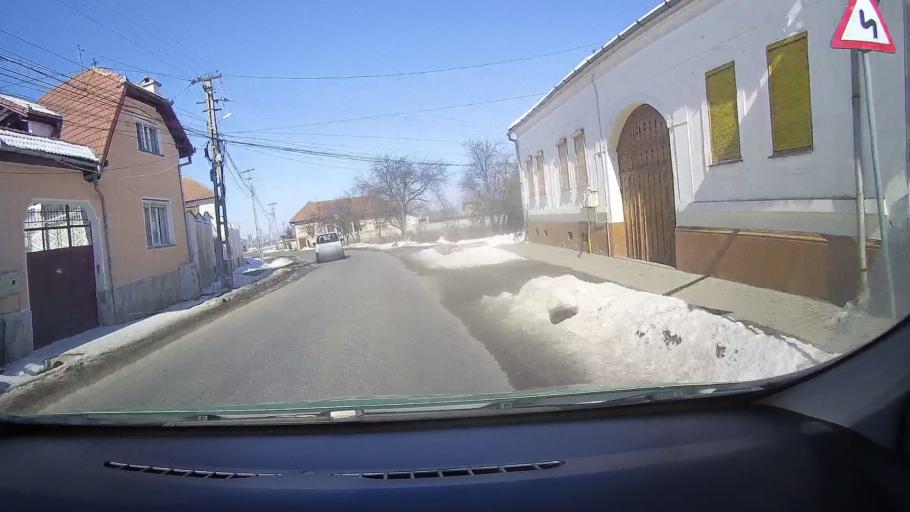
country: RO
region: Brasov
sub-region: Comuna Harseni
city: Harseni
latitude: 45.7921
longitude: 24.9967
